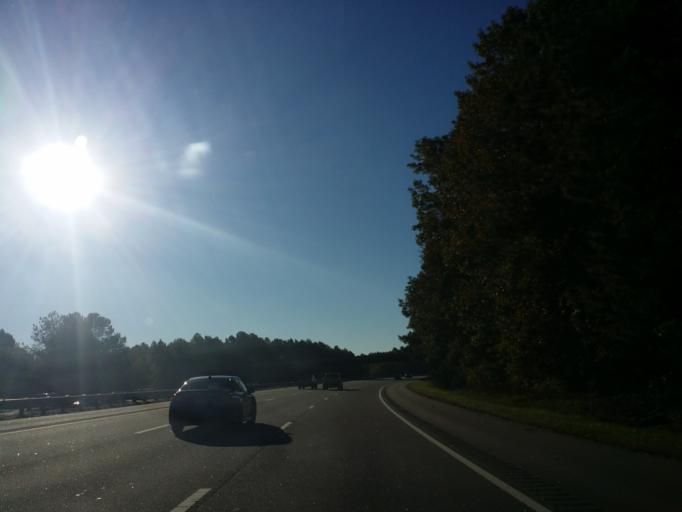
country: US
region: North Carolina
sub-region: Wake County
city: Cary
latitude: 35.8184
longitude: -78.7406
